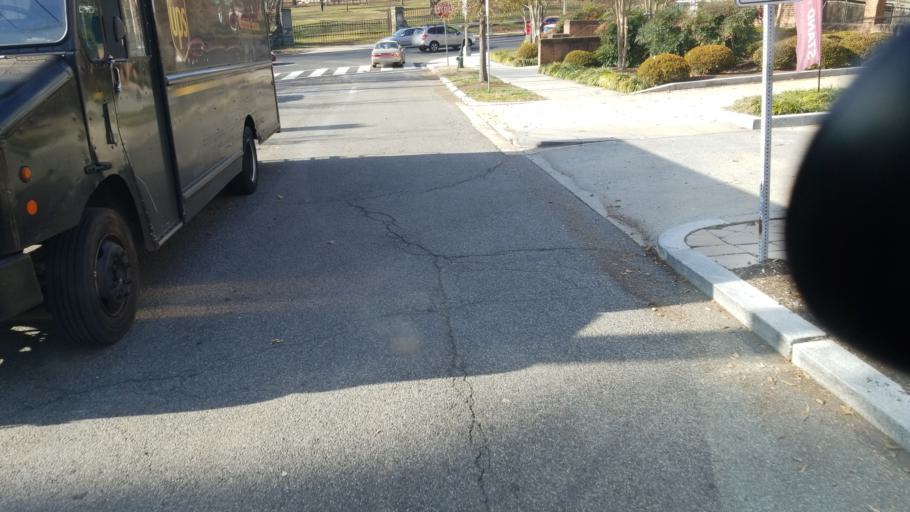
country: US
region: Maryland
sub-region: Montgomery County
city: Chevy Chase Village
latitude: 38.9421
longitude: -77.0616
